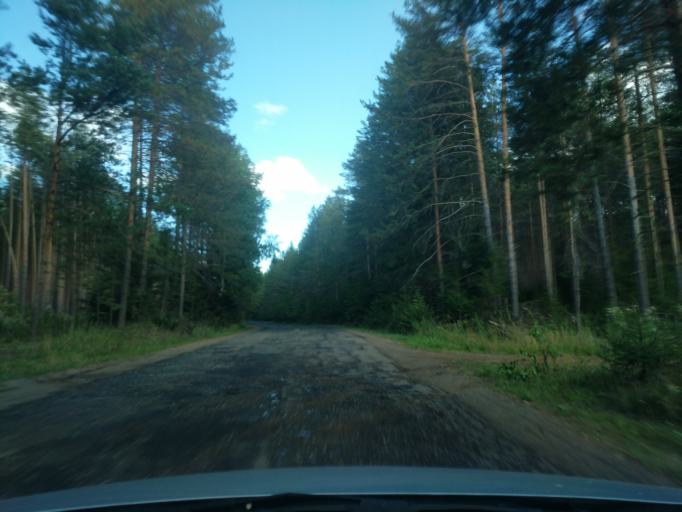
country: RU
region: Kirov
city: Kirovo-Chepetsk
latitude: 58.6059
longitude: 49.9233
